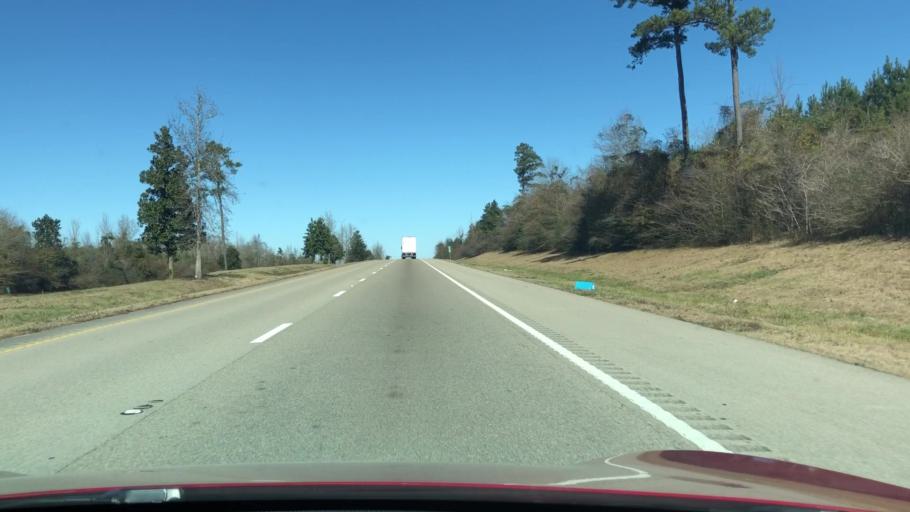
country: US
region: Mississippi
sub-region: Pearl River County
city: Poplarville
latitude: 30.7683
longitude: -89.5211
